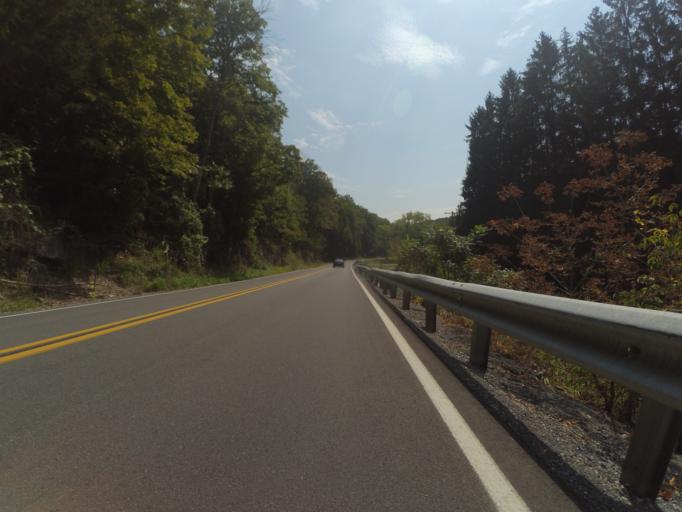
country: US
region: Pennsylvania
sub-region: Centre County
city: Bellefonte
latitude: 40.8918
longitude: -77.7633
